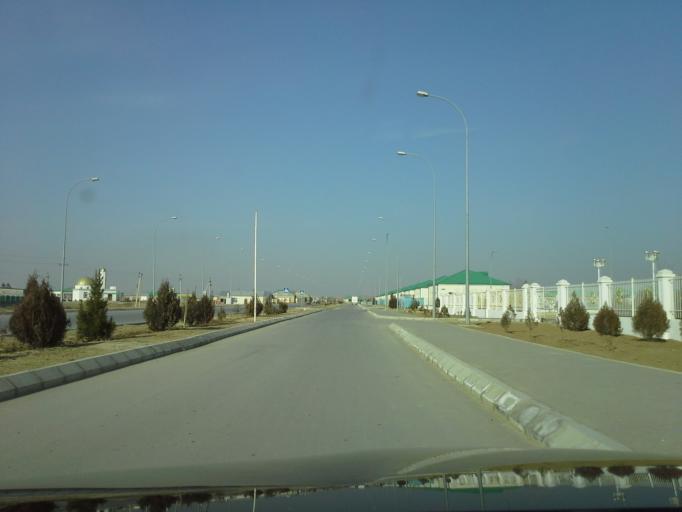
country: TM
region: Ahal
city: Abadan
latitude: 38.1708
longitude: 58.0467
